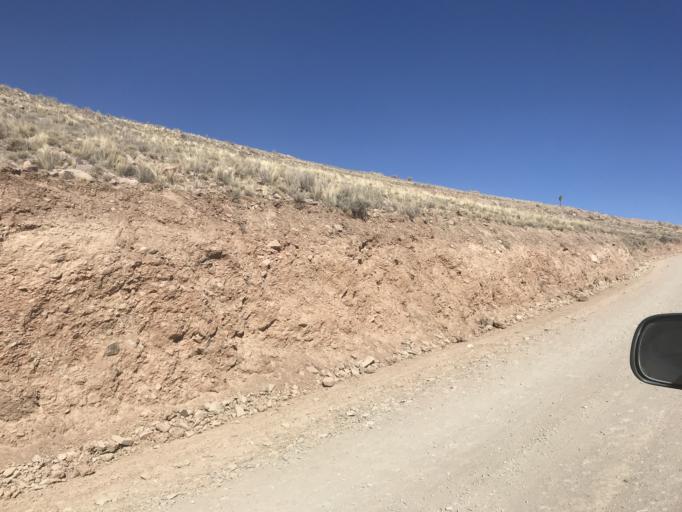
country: AR
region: Jujuy
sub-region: Departamento de Humahuaca
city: Humahuaca
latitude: -23.1962
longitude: -65.2247
